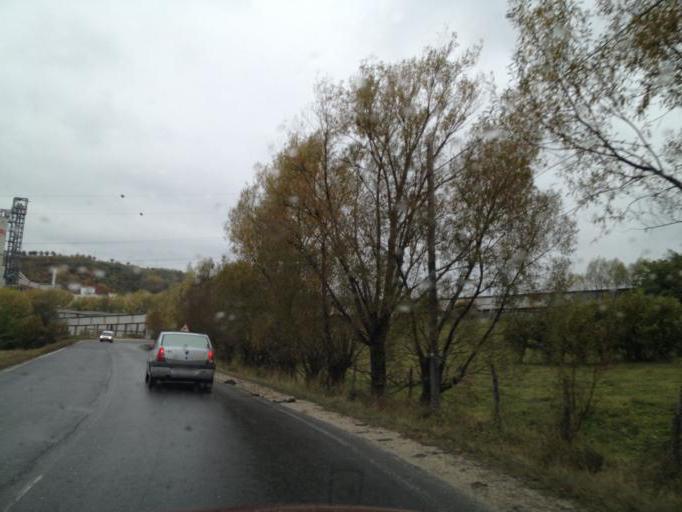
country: RO
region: Arges
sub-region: Comuna Valea Mare-Pravat
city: Valea Mare Pravat
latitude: 45.2925
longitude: 25.1165
